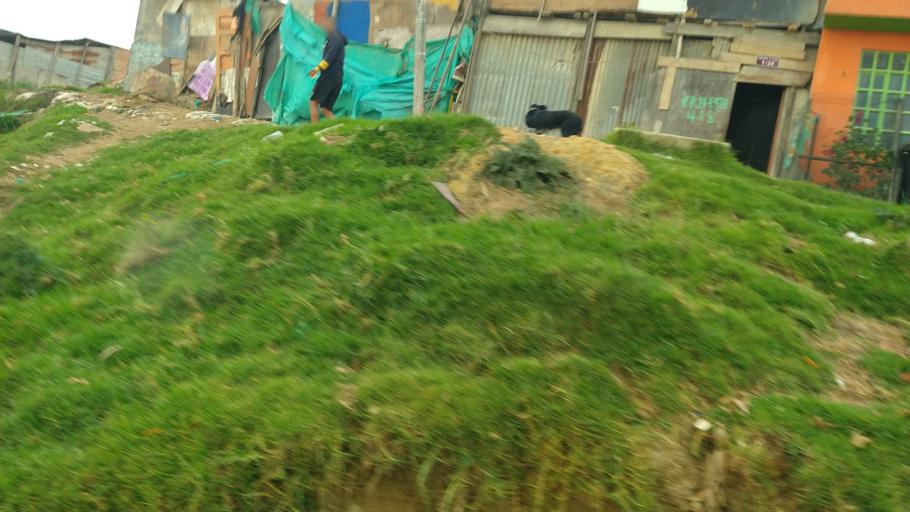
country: CO
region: Cundinamarca
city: Soacha
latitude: 4.5651
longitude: -74.2201
